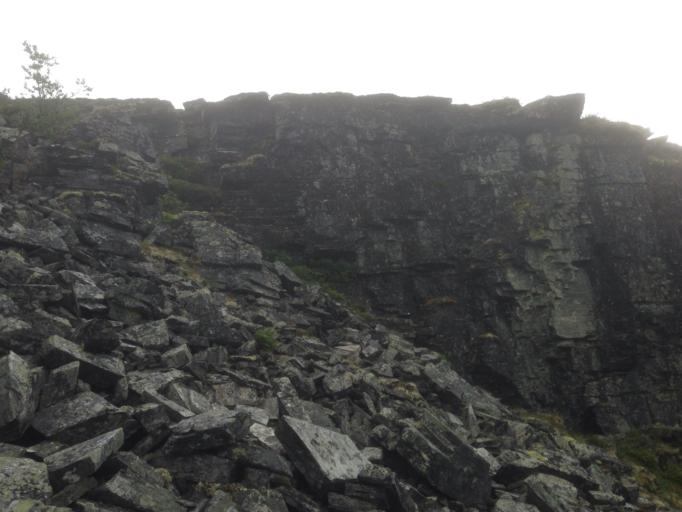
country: SE
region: Jaemtland
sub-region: Are Kommun
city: Are
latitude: 62.6937
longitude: 12.9389
